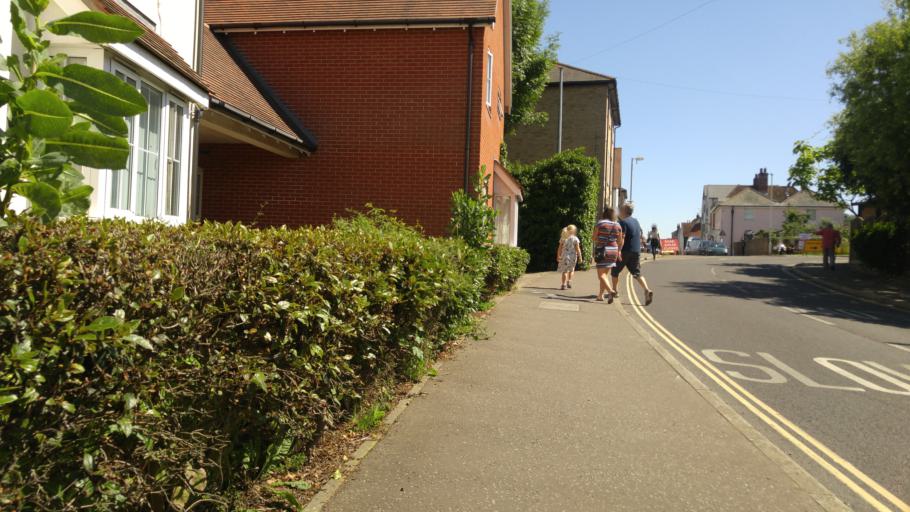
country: GB
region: England
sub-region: Essex
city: Rowhedge
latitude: 51.8584
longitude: 0.9477
